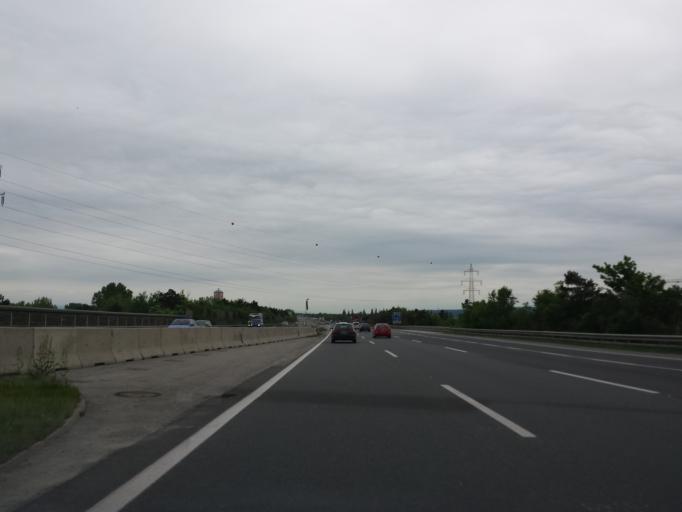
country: AT
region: Lower Austria
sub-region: Politischer Bezirk Baden
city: Leobersdorf
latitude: 47.9329
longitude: 16.2102
